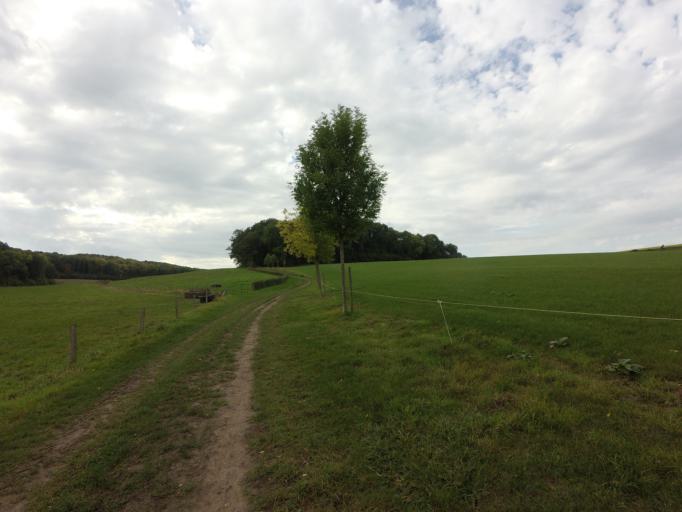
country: NL
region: Limburg
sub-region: Valkenburg aan de Geul
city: Schin op Geul
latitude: 50.8032
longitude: 5.9010
